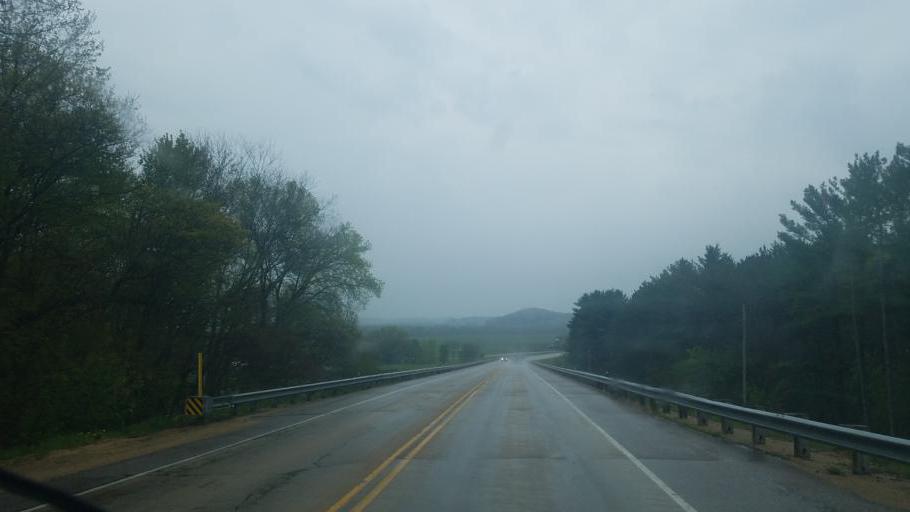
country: US
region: Wisconsin
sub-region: Sauk County
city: Reedsburg
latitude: 43.6026
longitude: -90.1348
